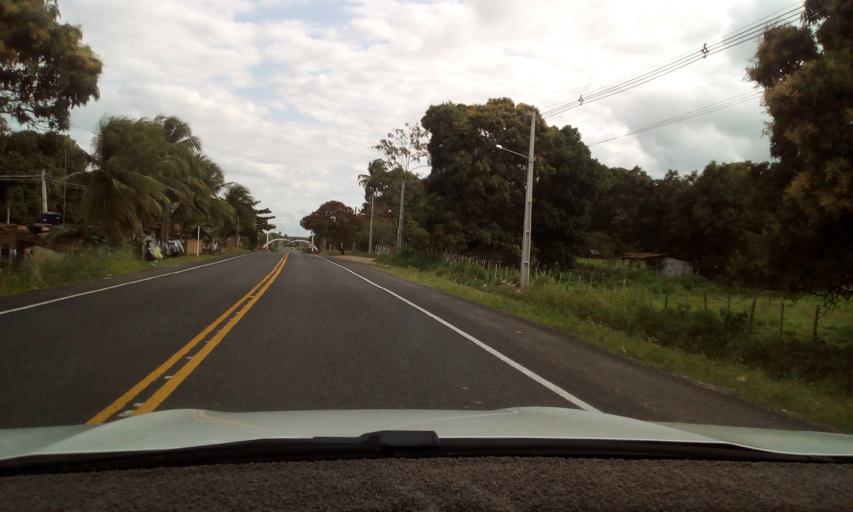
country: BR
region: Paraiba
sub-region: Mamanguape
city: Mamanguape
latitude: -6.8231
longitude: -35.1082
